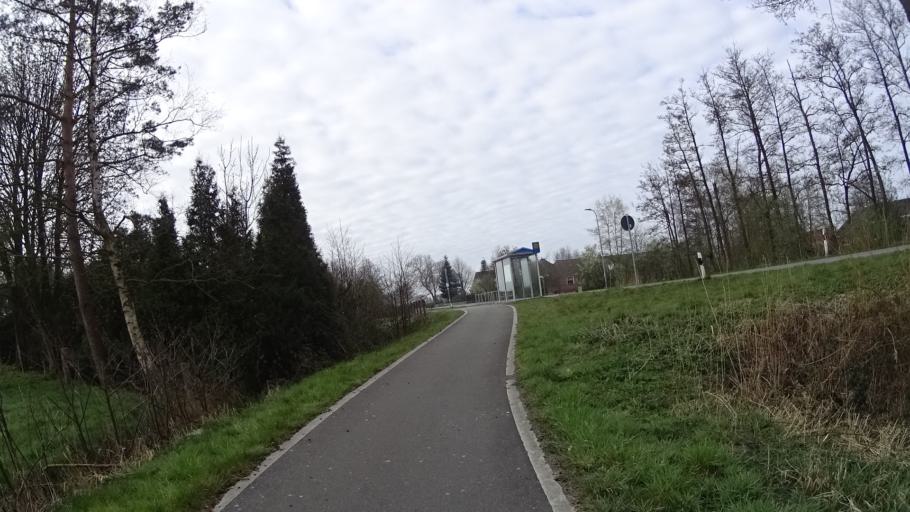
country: DE
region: Lower Saxony
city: Upgant-Schott
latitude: 53.4317
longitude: 7.3200
